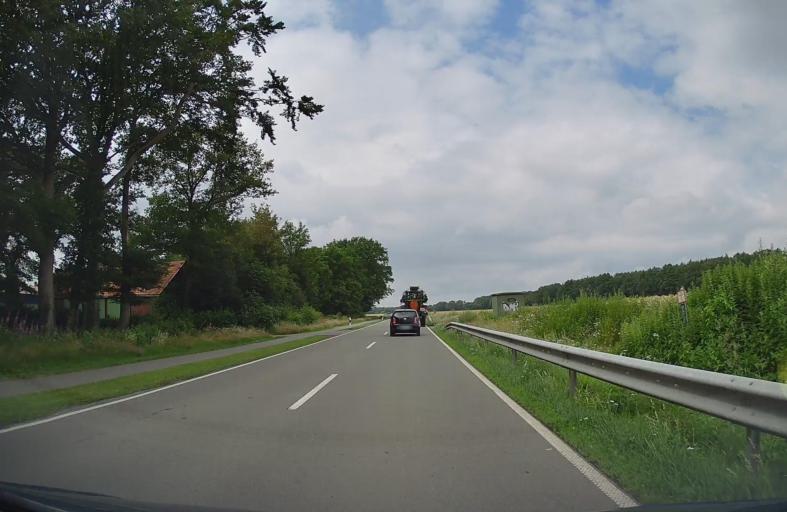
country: DE
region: Lower Saxony
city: Friesoythe
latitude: 53.0472
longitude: 7.8230
